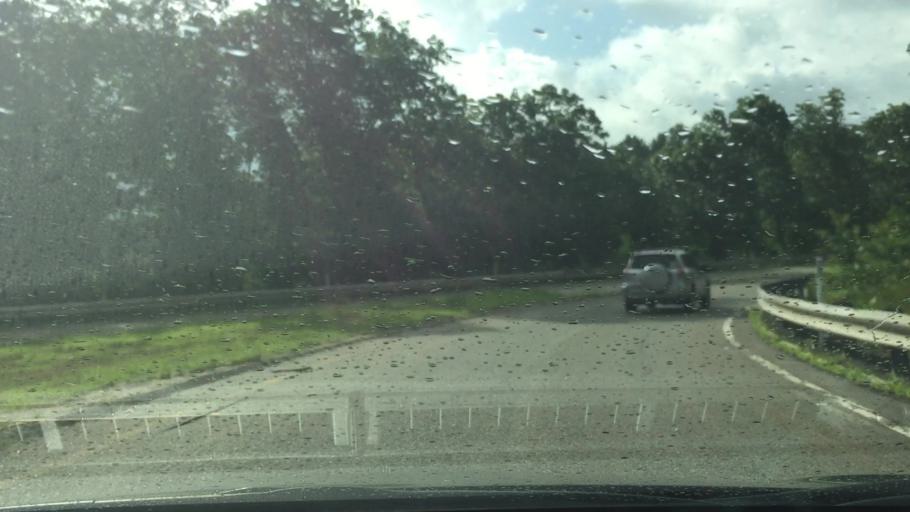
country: US
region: Massachusetts
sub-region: Worcester County
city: Harvard
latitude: 42.4882
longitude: -71.5427
